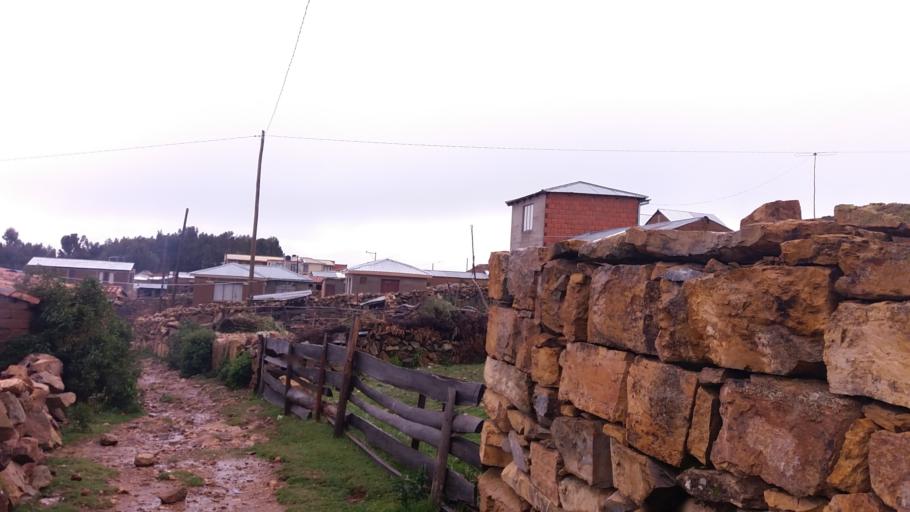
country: BO
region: La Paz
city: Yumani
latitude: -16.0347
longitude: -69.1509
